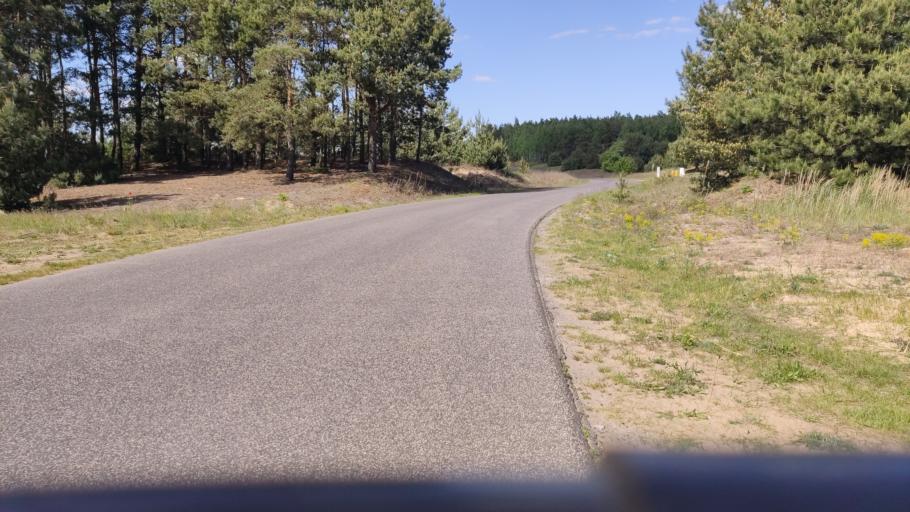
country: PL
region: Kujawsko-Pomorskie
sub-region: Wloclawek
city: Wloclawek
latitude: 52.5864
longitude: 19.0917
